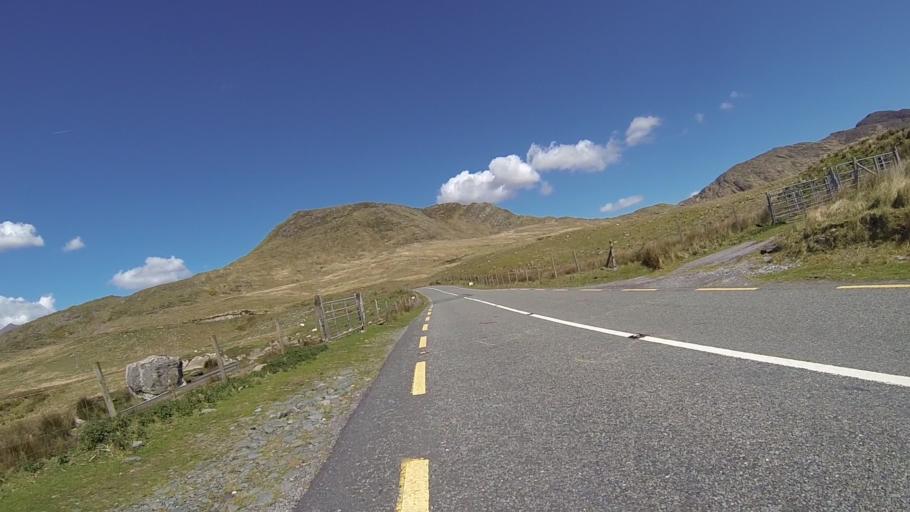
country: IE
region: Munster
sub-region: Ciarrai
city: Kenmare
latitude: 51.9283
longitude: -9.6465
